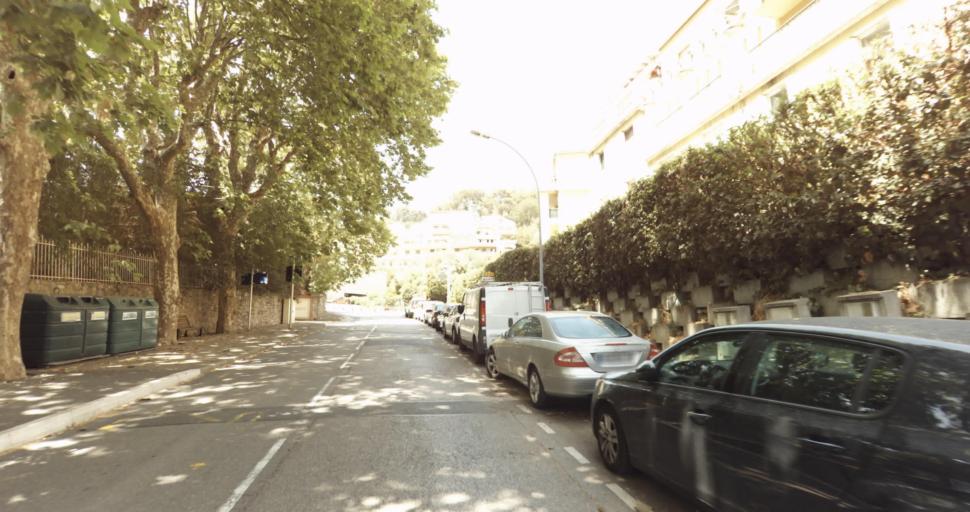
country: FR
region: Provence-Alpes-Cote d'Azur
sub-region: Departement des Alpes-Maritimes
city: Roquebrune-Cap-Martin
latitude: 43.7778
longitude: 7.4717
